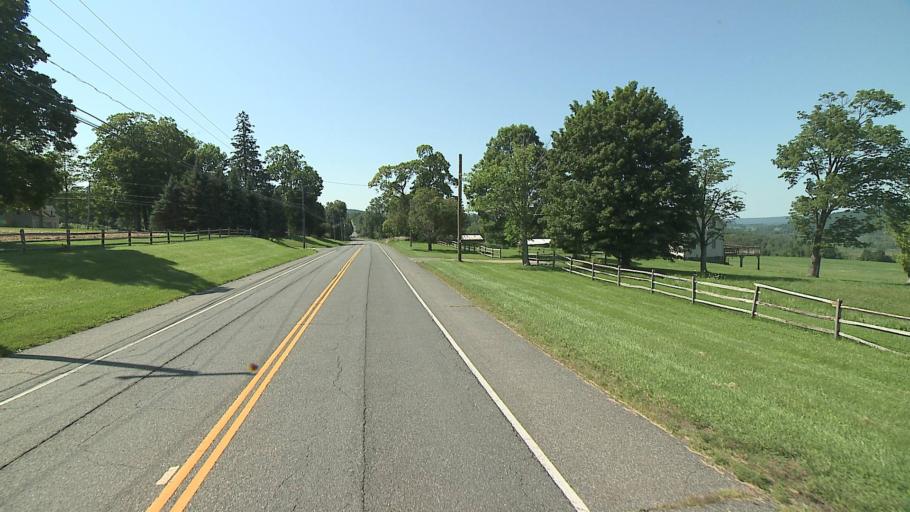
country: US
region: Connecticut
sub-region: Litchfield County
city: Canaan
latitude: 41.9187
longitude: -73.4452
